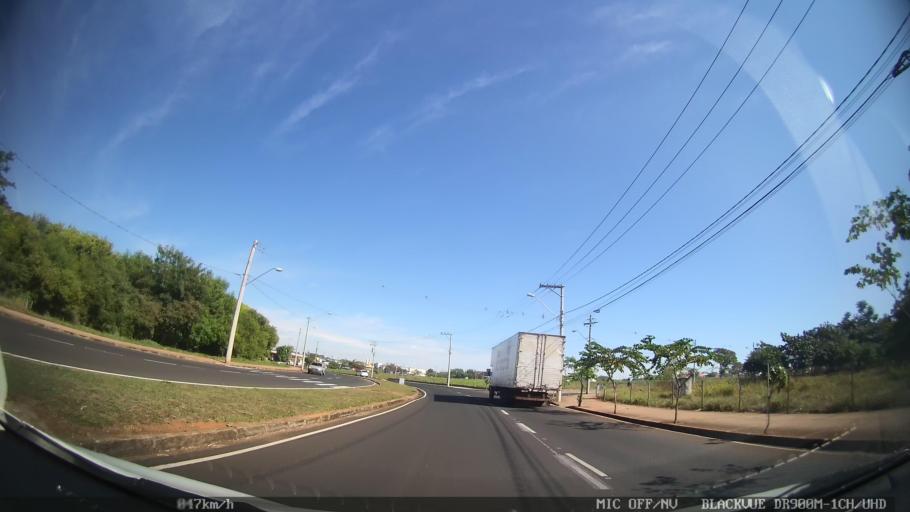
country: BR
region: Sao Paulo
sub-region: Sao Jose Do Rio Preto
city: Sao Jose do Rio Preto
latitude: -20.8048
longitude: -49.4244
